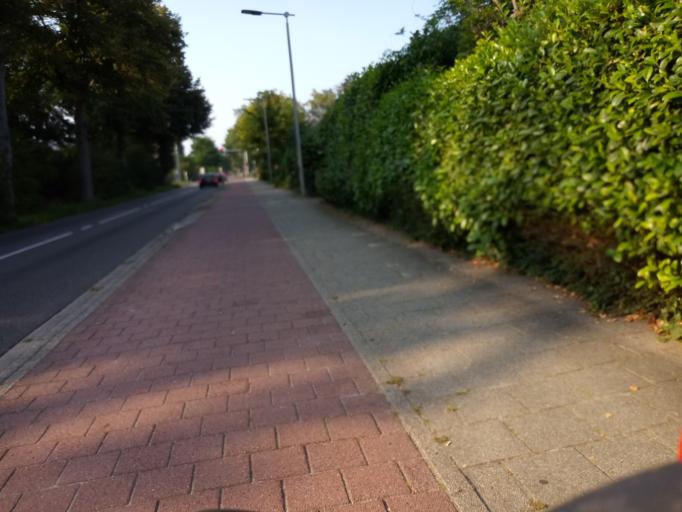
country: NL
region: Gelderland
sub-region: Gemeente Rozendaal
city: Rozendaal
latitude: 51.9918
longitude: 5.9494
